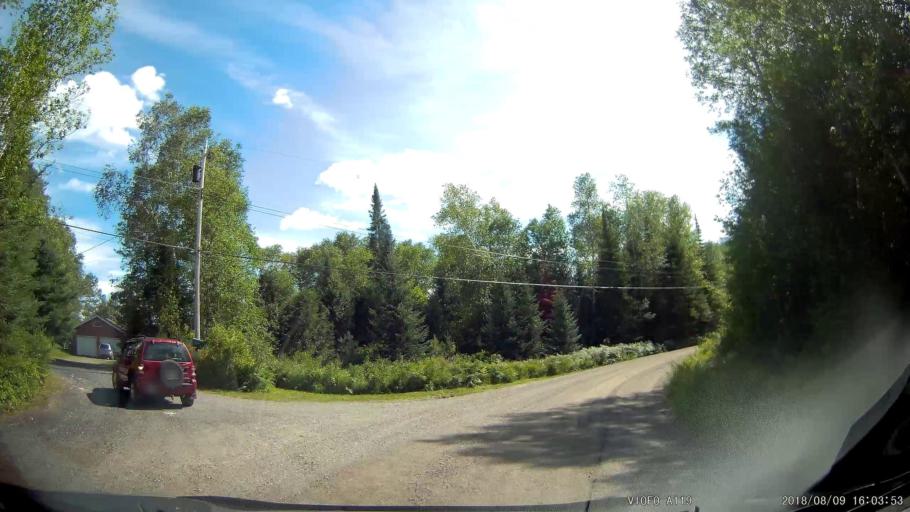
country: CA
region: Ontario
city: Rayside-Balfour
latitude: 46.6077
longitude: -81.4639
